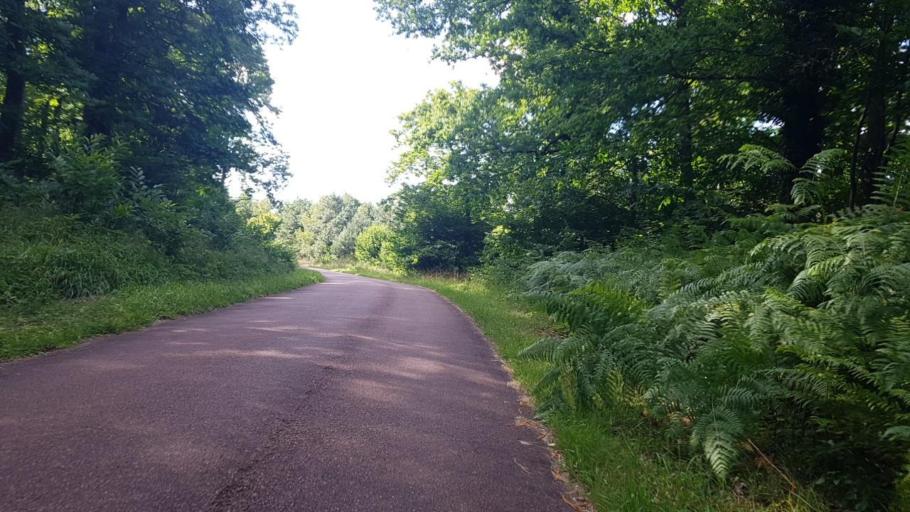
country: FR
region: Picardie
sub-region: Departement de l'Oise
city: Chamant
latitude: 49.1733
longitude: 2.6284
